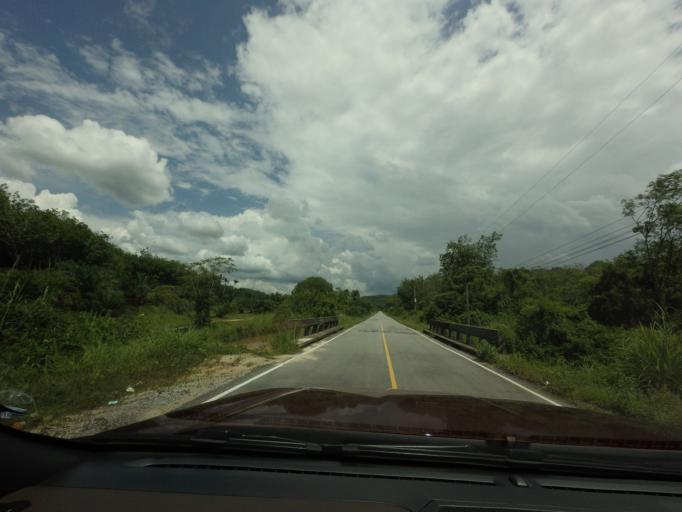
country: TH
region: Narathiwat
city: Chanae
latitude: 6.0623
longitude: 101.6877
